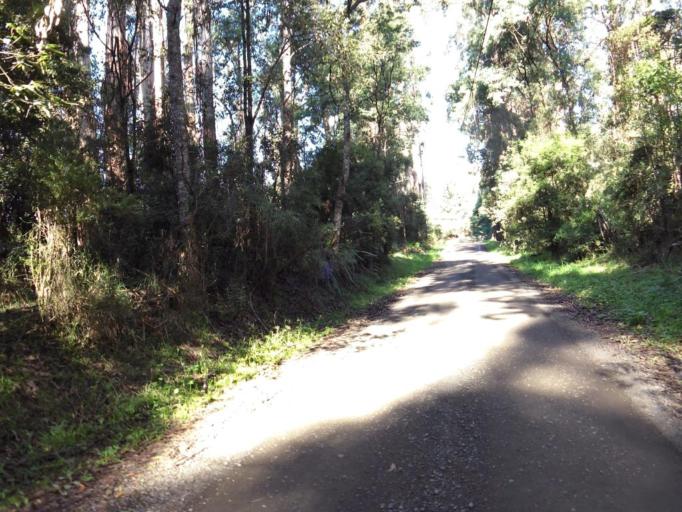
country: AU
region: Victoria
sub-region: Cardinia
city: Emerald
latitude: -37.9161
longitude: 145.4392
